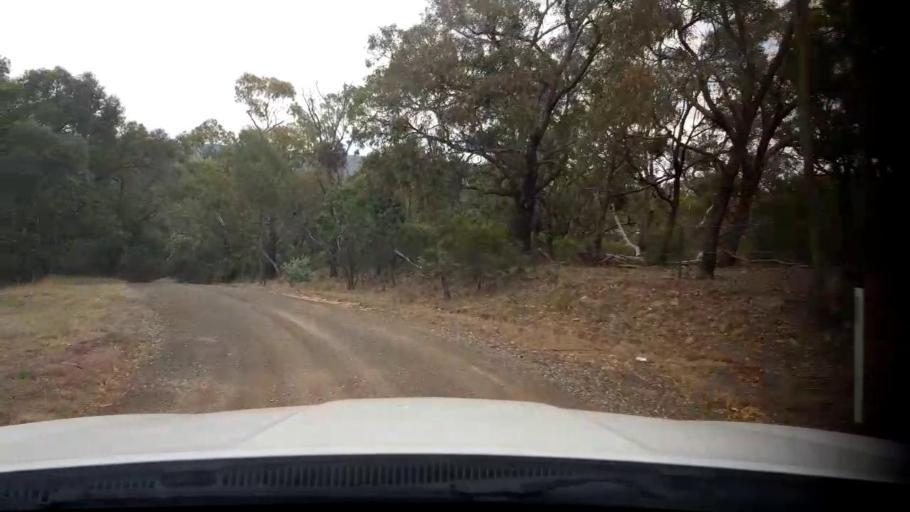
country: AU
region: Victoria
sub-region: Whittlesea
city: Whittlesea
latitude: -37.4891
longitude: 145.0495
